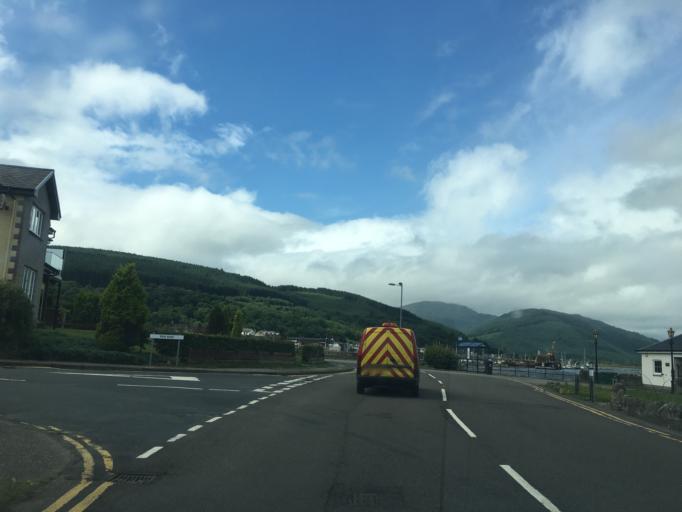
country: GB
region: Scotland
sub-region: Argyll and Bute
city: Dunoon
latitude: 55.9808
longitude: -4.9401
